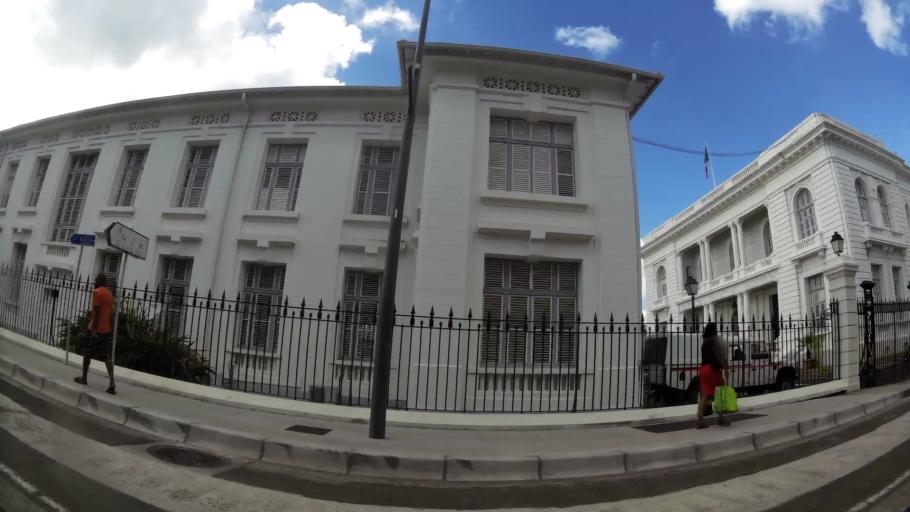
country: MQ
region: Martinique
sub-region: Martinique
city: Fort-de-France
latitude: 14.6052
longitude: -61.0677
